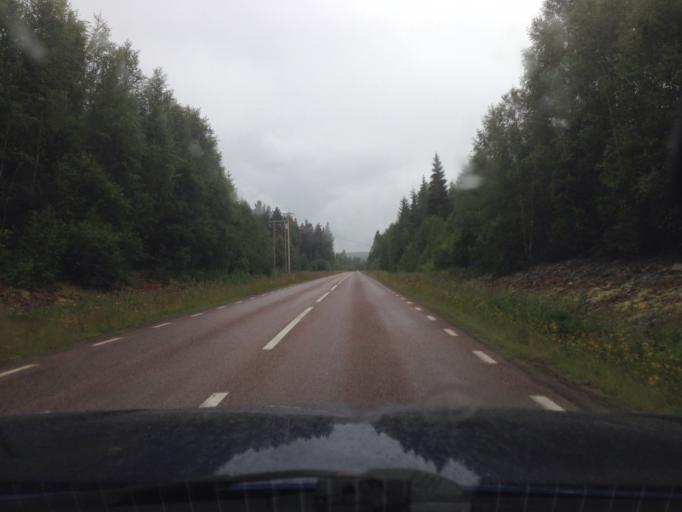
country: SE
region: Dalarna
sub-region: Ludvika Kommun
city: Grangesberg
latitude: 60.1317
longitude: 15.0530
